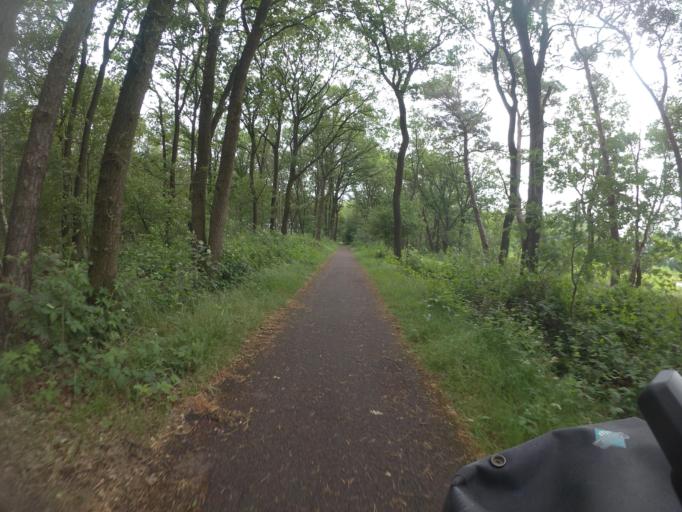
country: NL
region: Drenthe
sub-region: Gemeente Hoogeveen
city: Hoogeveen
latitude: 52.8349
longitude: 6.4877
